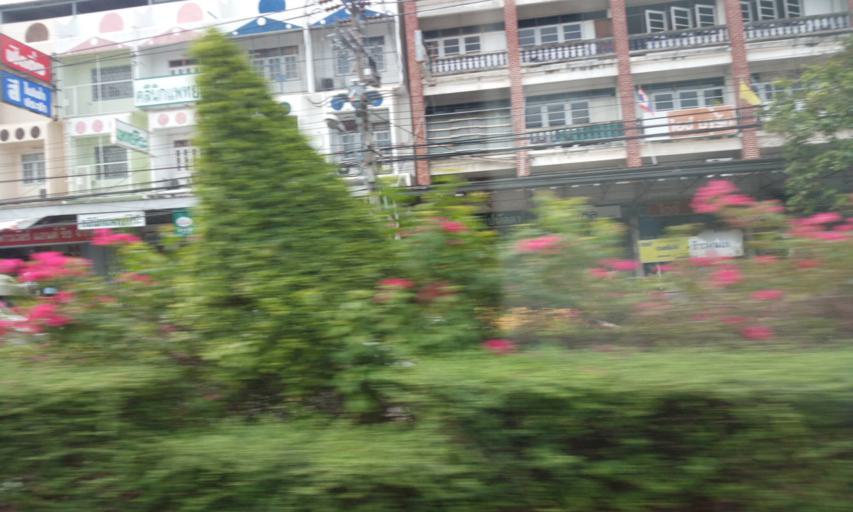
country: TH
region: Bangkok
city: Saphan Sung
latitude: 13.7221
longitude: 100.7106
